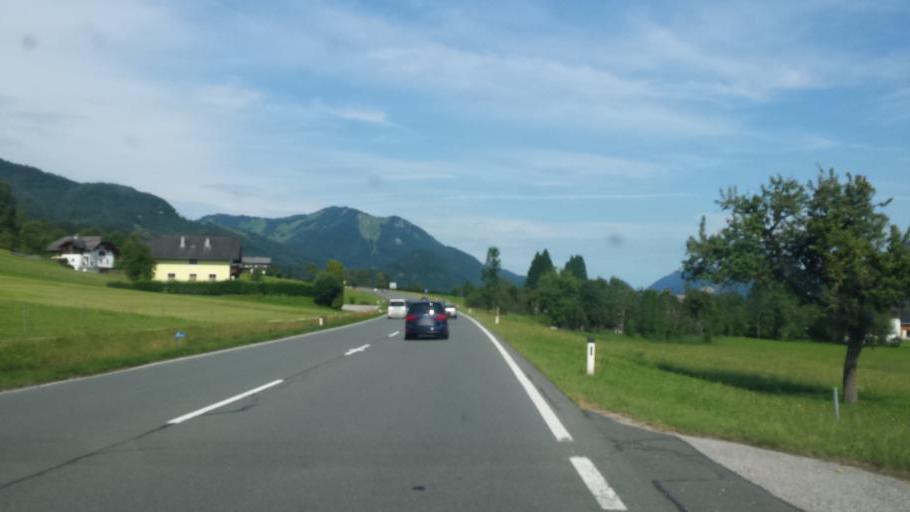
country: AT
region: Upper Austria
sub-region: Politischer Bezirk Gmunden
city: Sankt Wolfgang im Salzkammergut
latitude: 47.7155
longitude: 13.4464
